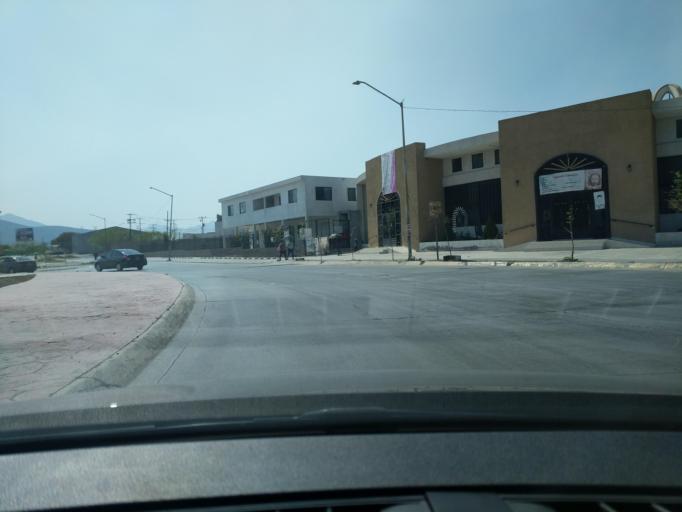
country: MX
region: Nuevo Leon
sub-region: Garcia
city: Valle de Lincoln
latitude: 25.7909
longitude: -100.4898
